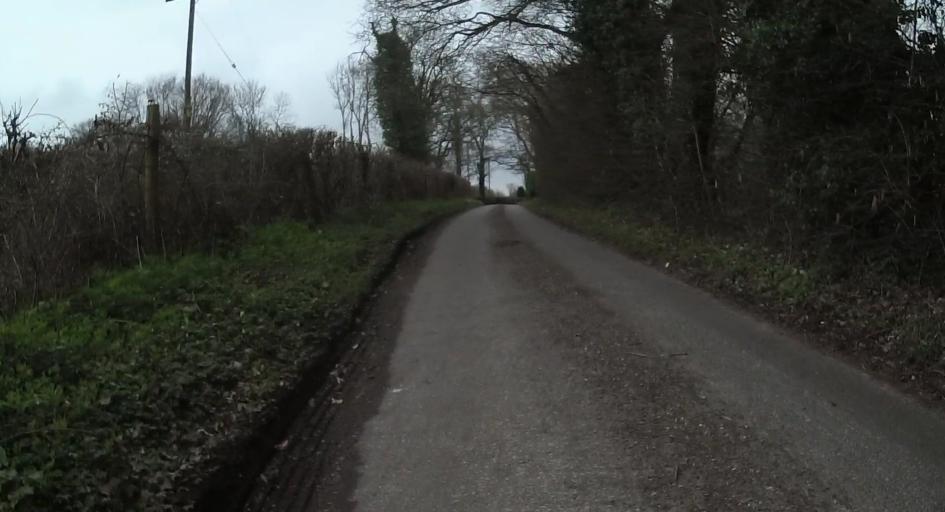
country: GB
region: England
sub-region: Hampshire
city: Four Marks
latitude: 51.0948
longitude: -1.1007
